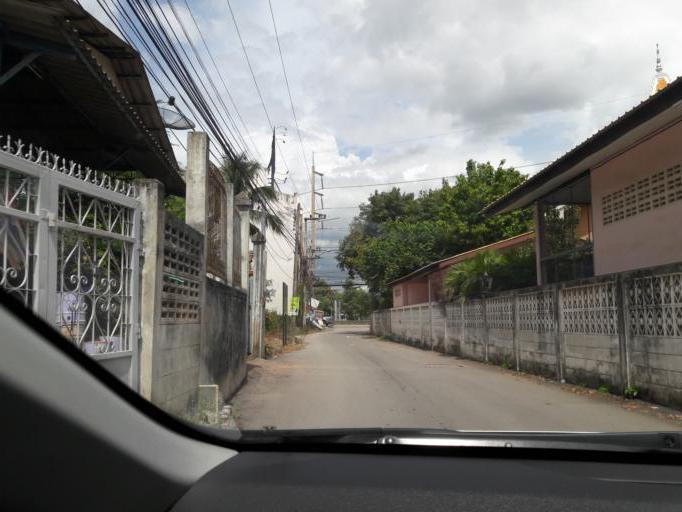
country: TH
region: Ratchaburi
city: Ratchaburi
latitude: 13.5331
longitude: 99.7938
